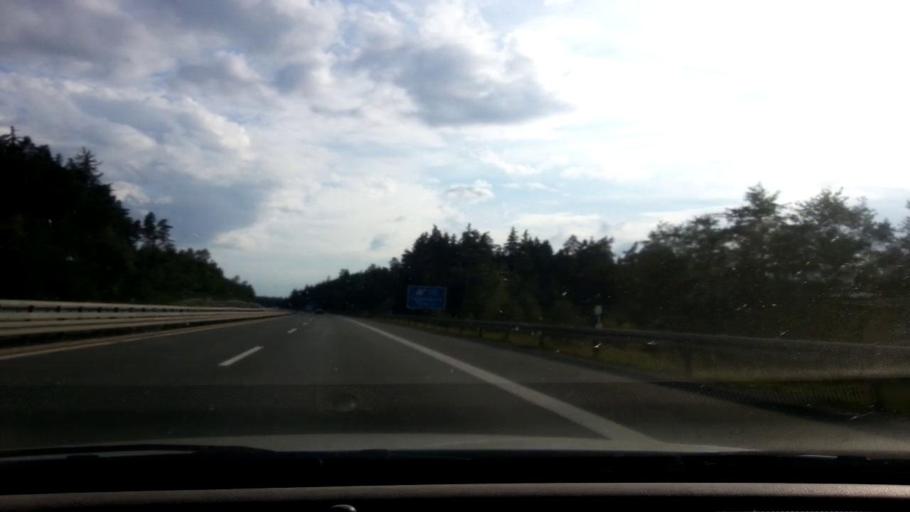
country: DE
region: Bavaria
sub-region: Upper Palatinate
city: Wiesau
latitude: 49.8708
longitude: 12.1882
